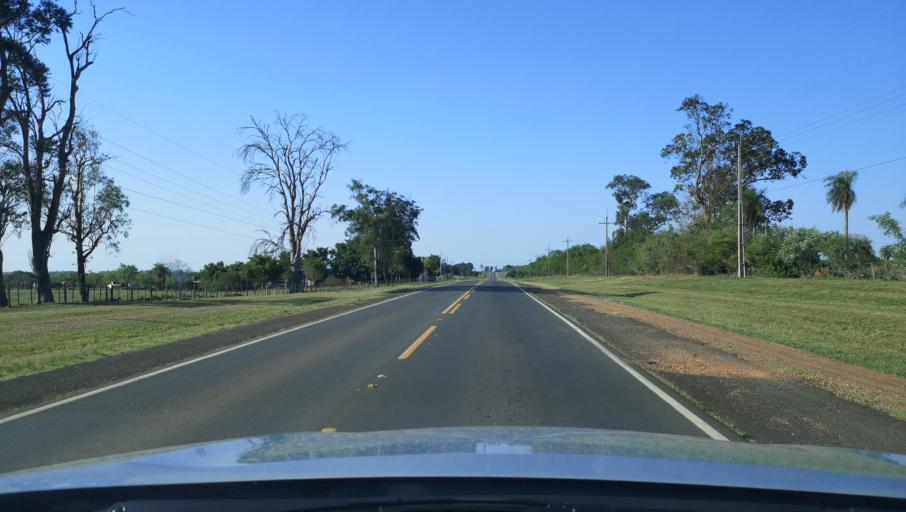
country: PY
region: Misiones
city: Santa Maria
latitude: -26.8228
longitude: -57.0274
